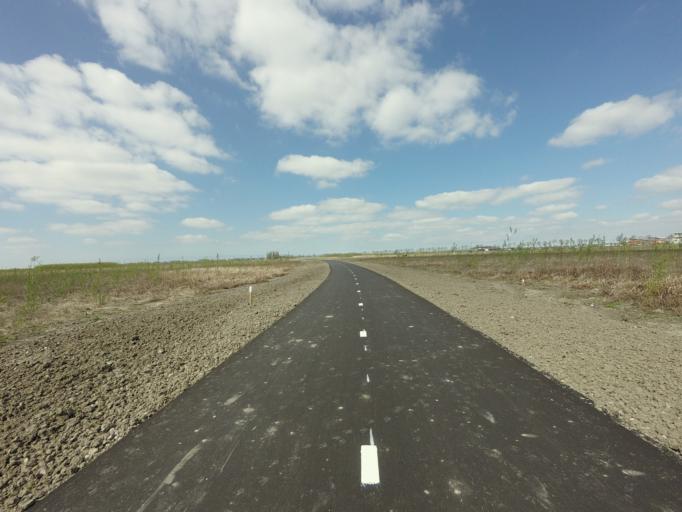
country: NL
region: South Holland
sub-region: Gemeente Waddinxveen
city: Groenswaard
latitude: 52.0715
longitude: 4.6239
